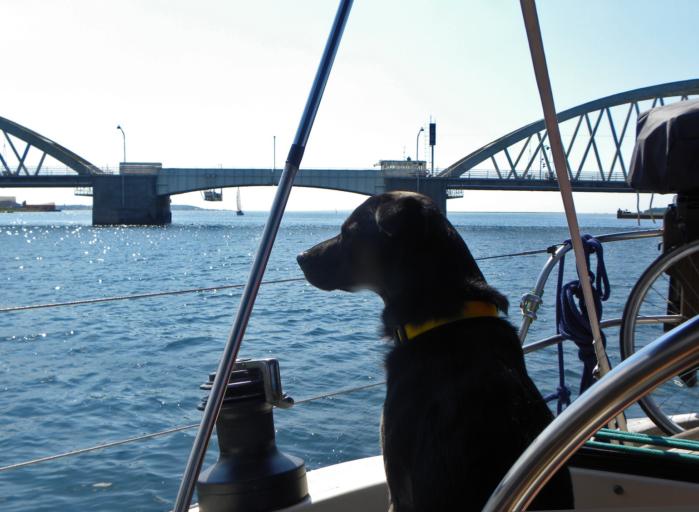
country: DK
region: North Denmark
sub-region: Vesthimmerland Kommune
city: Logstor
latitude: 56.9997
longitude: 9.2942
